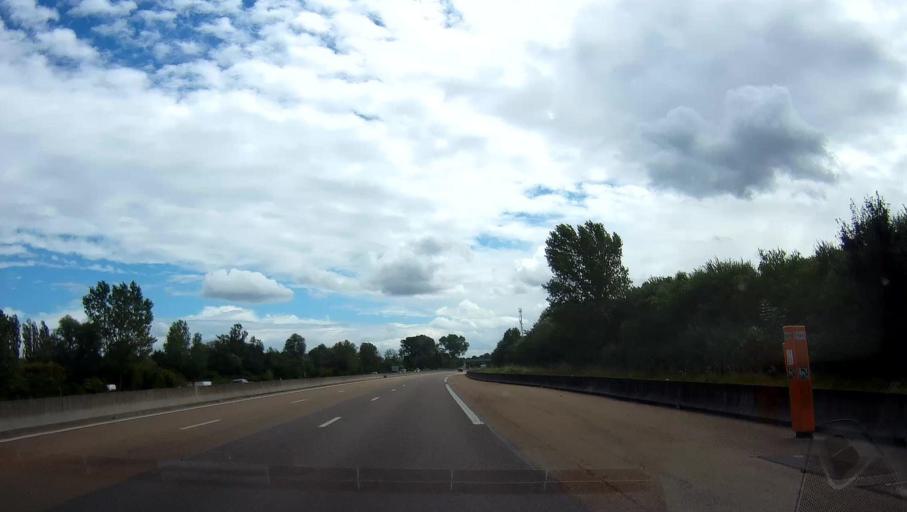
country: FR
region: Bourgogne
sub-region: Departement de la Cote-d'Or
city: Saint-Julien
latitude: 47.4069
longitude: 5.1810
